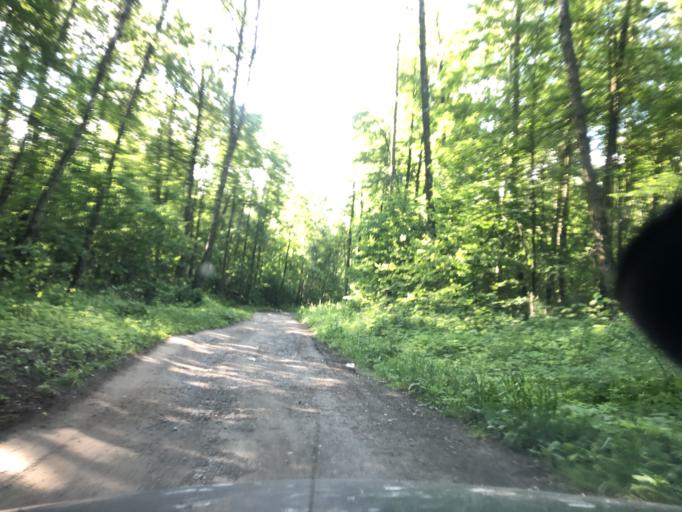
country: RU
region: Tula
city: Shvartsevskiy
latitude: 54.2560
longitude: 37.9235
